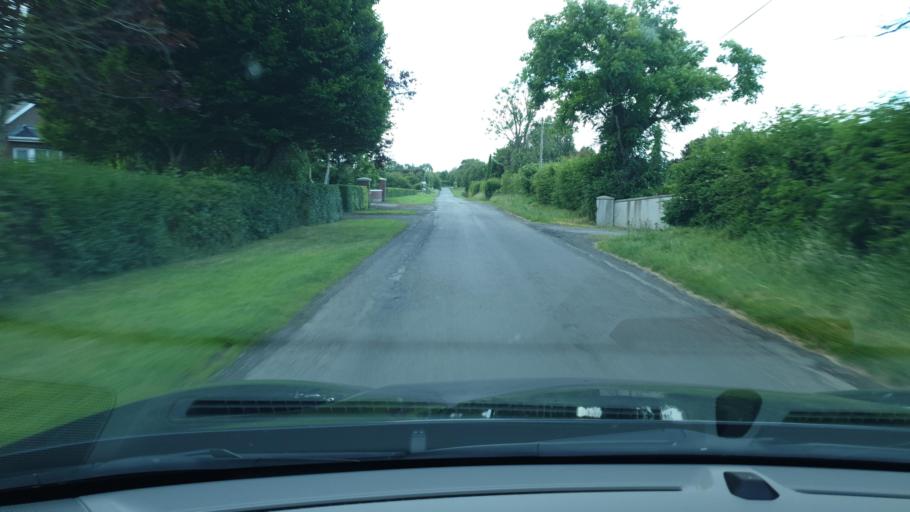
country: IE
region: Leinster
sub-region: An Mhi
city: Ratoath
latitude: 53.5669
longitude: -6.4948
